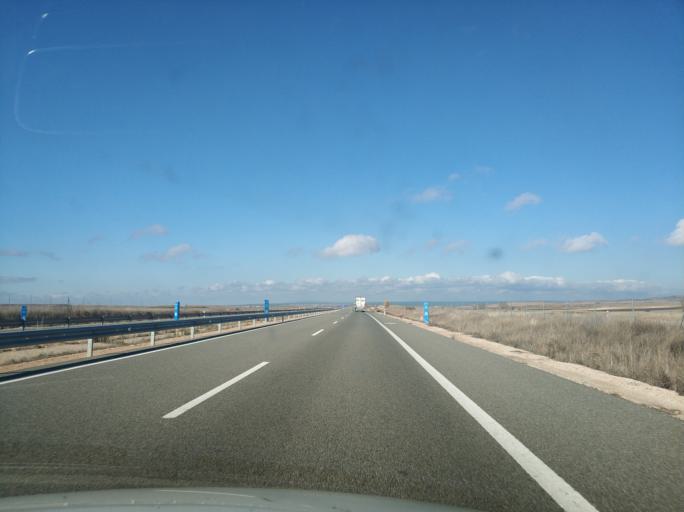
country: ES
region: Castille and Leon
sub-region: Provincia de Soria
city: Coscurita
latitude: 41.4016
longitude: -2.4779
